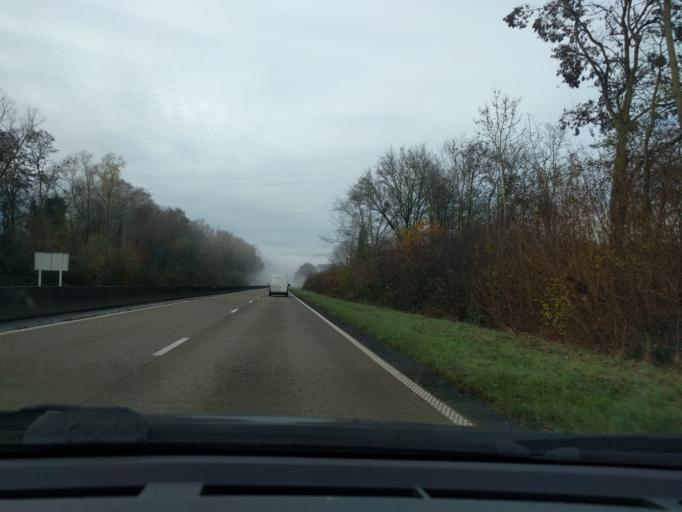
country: BE
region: Wallonia
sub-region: Province de Namur
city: Dinant
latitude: 50.2385
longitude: 4.9435
